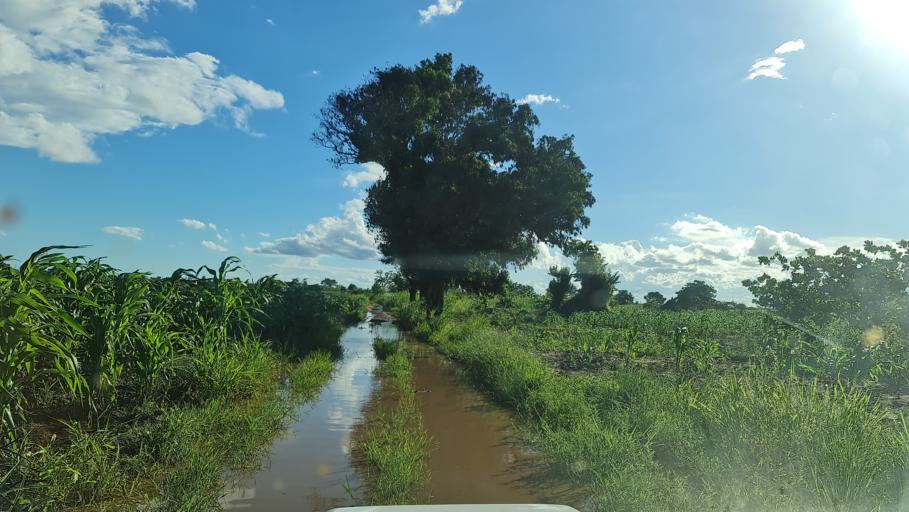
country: MZ
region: Nampula
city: Ilha de Mocambique
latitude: -14.9377
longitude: 40.2021
